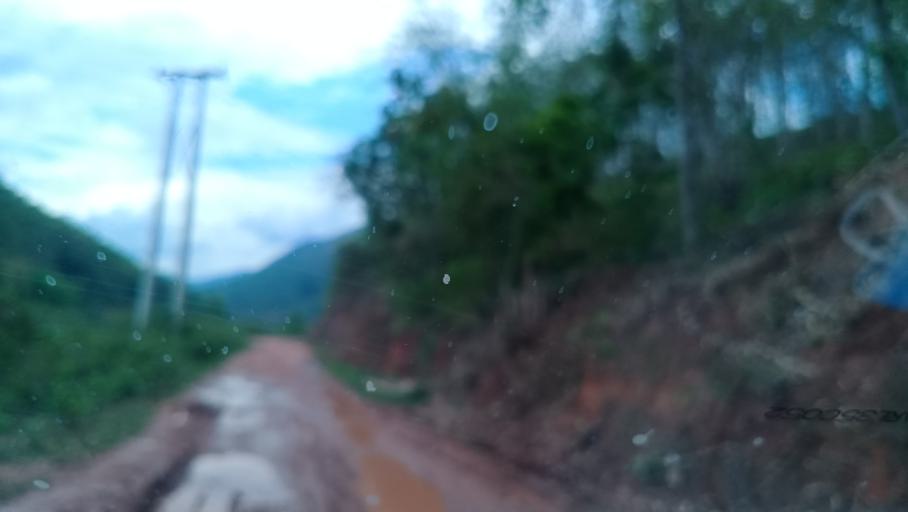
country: CN
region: Yunnan
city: Menglie
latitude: 22.1741
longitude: 101.7448
